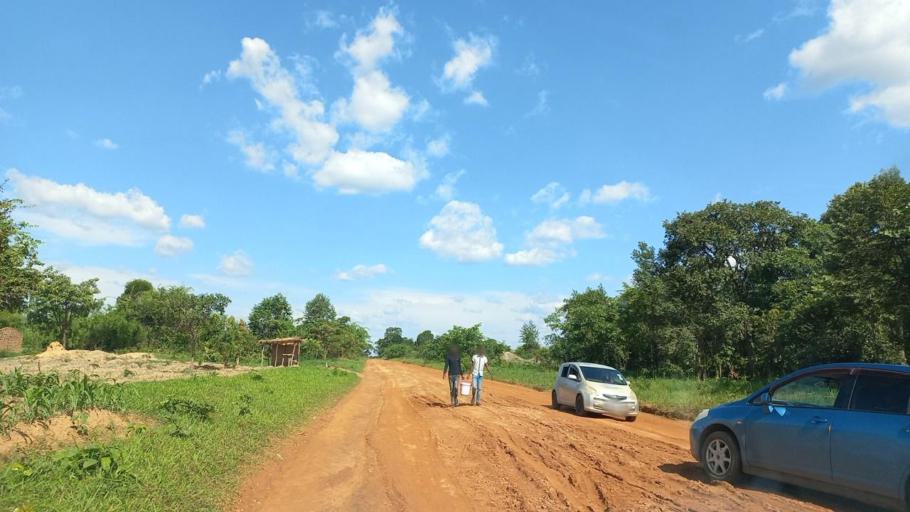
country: ZM
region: Copperbelt
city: Kitwe
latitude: -12.8704
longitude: 28.3484
